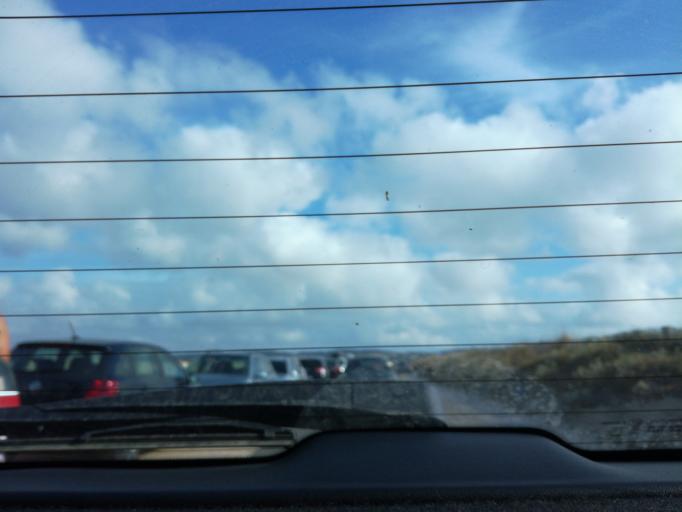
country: FR
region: Provence-Alpes-Cote d'Azur
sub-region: Departement du Var
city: Hyeres
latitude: 43.0621
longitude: 6.1320
